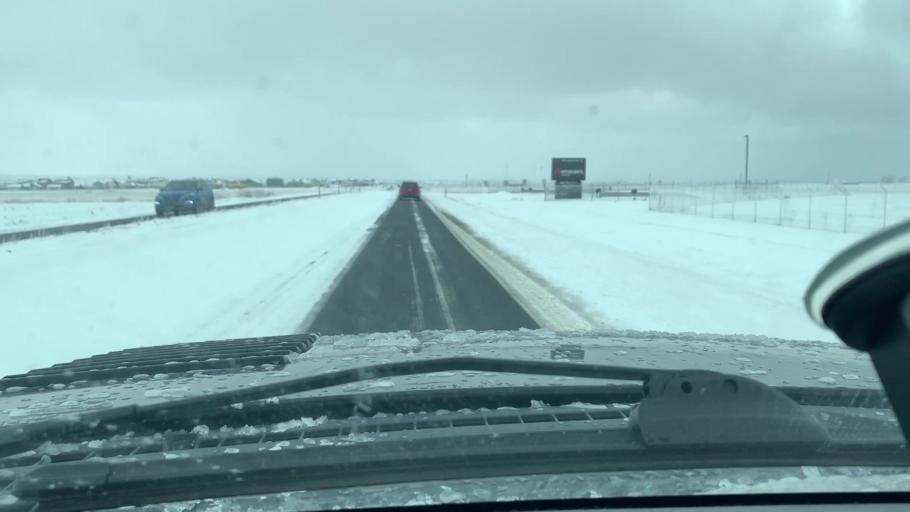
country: US
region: Colorado
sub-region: Weld County
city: Mead
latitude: 40.1946
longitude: -104.9702
